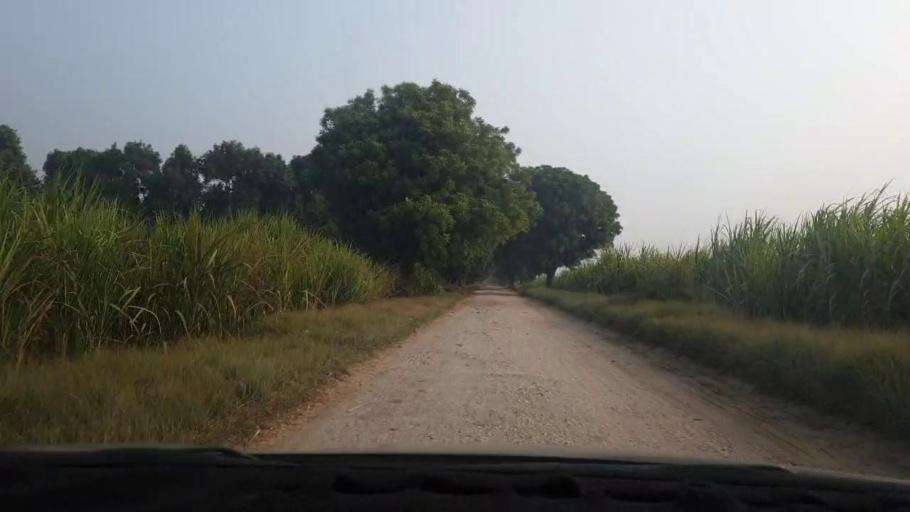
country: PK
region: Sindh
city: Matiari
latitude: 25.5833
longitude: 68.5185
